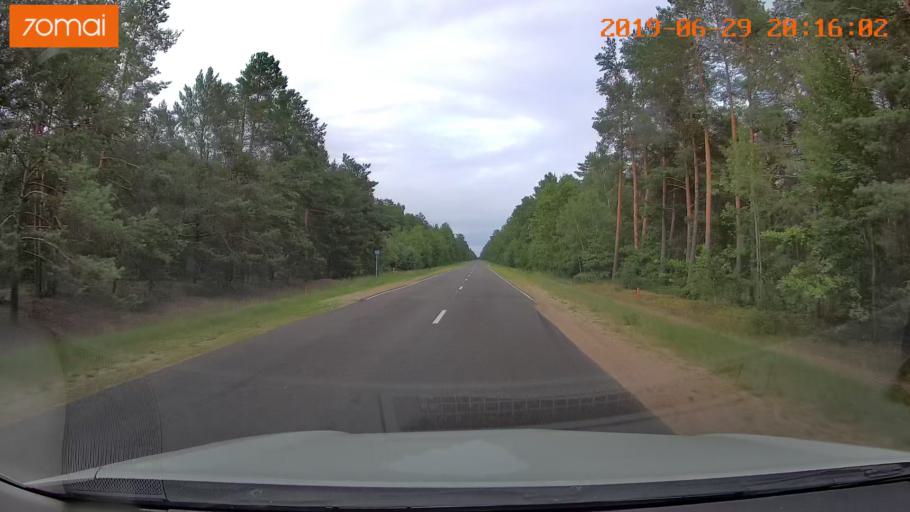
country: BY
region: Brest
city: Asnyezhytsy
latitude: 52.3784
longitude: 26.1881
